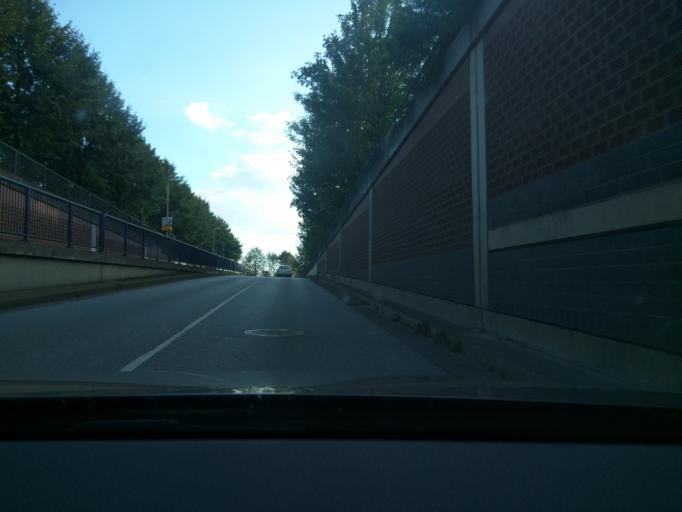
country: DE
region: Schleswig-Holstein
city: Schwarzenbek
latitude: 53.5023
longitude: 10.4892
